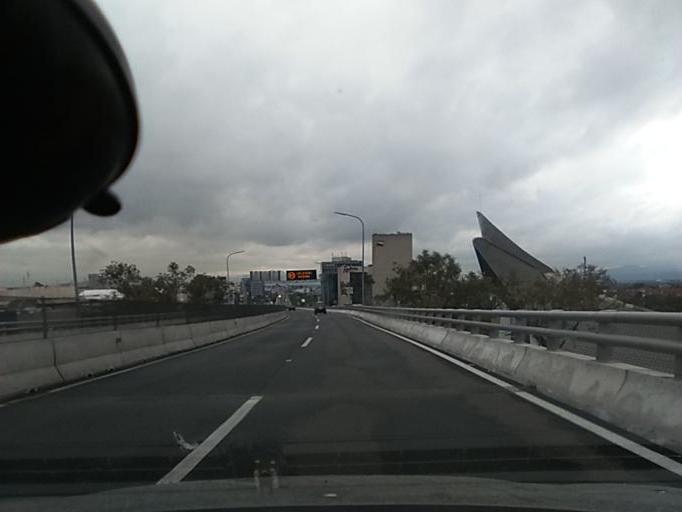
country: MX
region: Mexico City
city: Tlalpan
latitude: 19.3020
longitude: -99.1943
